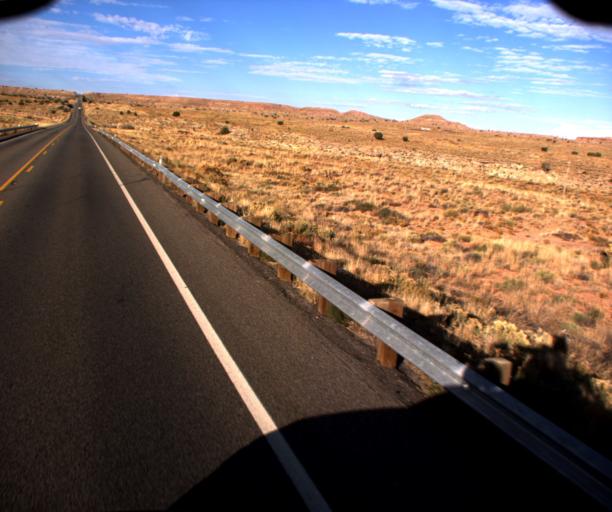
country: US
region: New Mexico
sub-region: San Juan County
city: Shiprock
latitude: 36.9342
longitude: -109.1336
